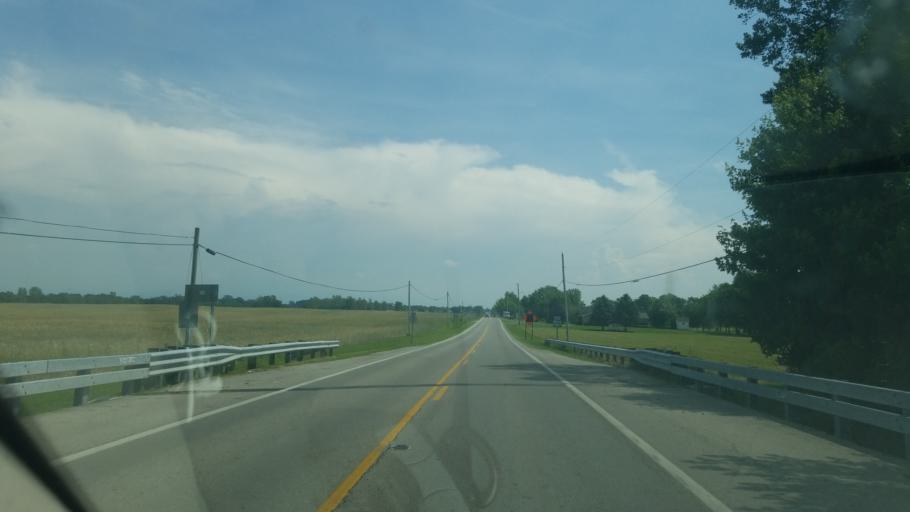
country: US
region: Ohio
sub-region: Logan County
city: Northwood
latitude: 40.5036
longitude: -83.7436
